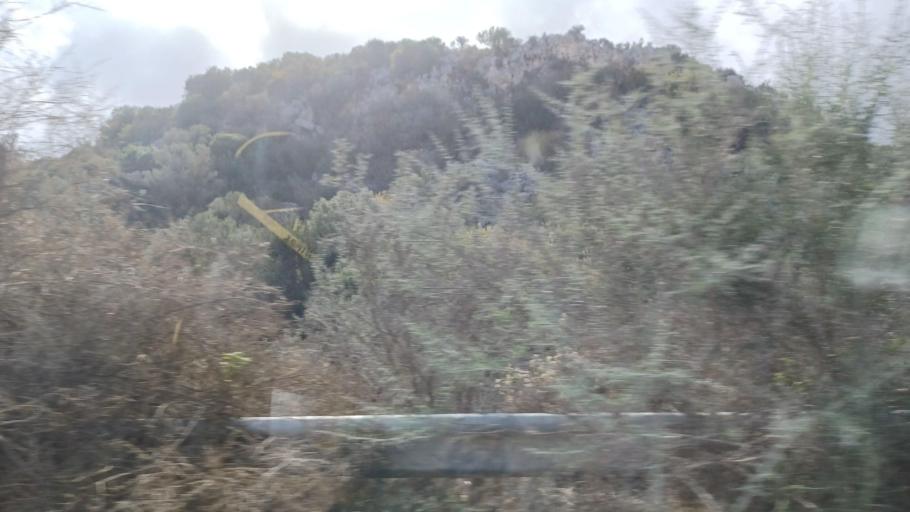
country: CY
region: Pafos
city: Polis
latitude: 34.9984
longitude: 32.4005
